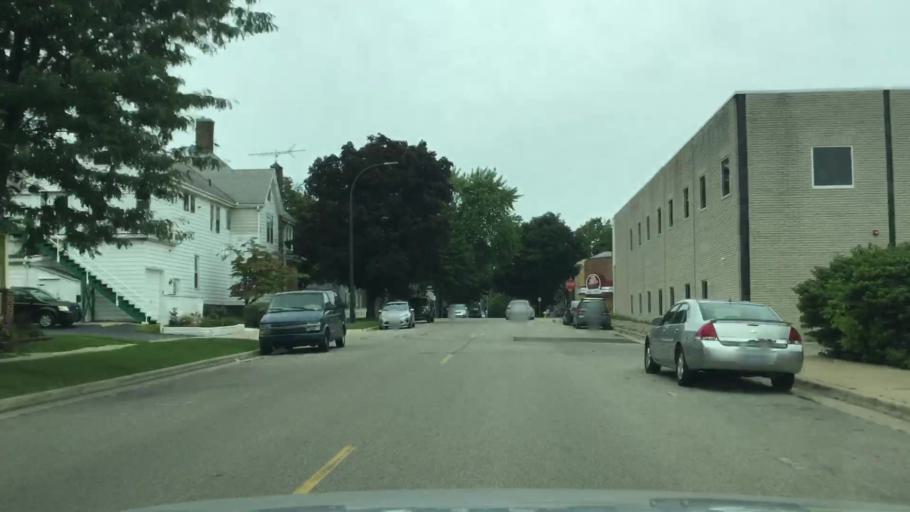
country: US
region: Michigan
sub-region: Washtenaw County
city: Ypsilanti
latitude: 42.2398
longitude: -83.6136
